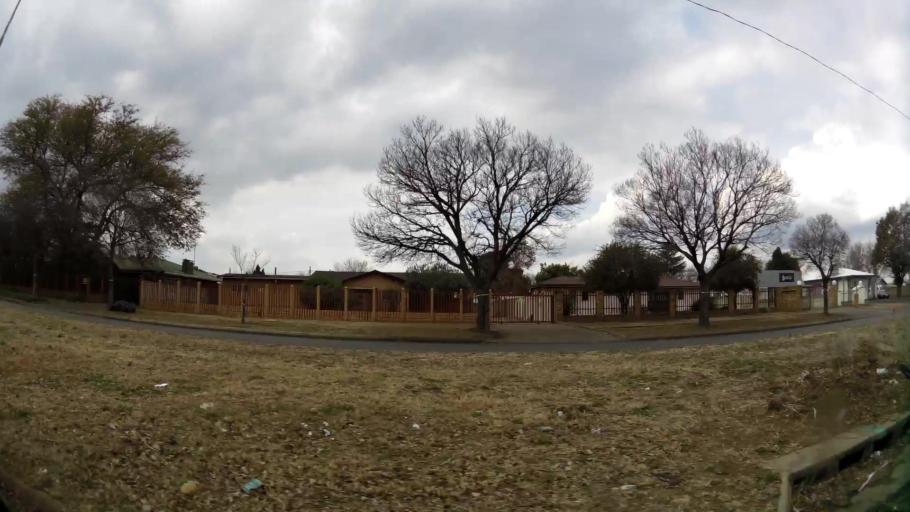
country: ZA
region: Gauteng
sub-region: Sedibeng District Municipality
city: Vanderbijlpark
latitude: -26.7184
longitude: 27.8241
